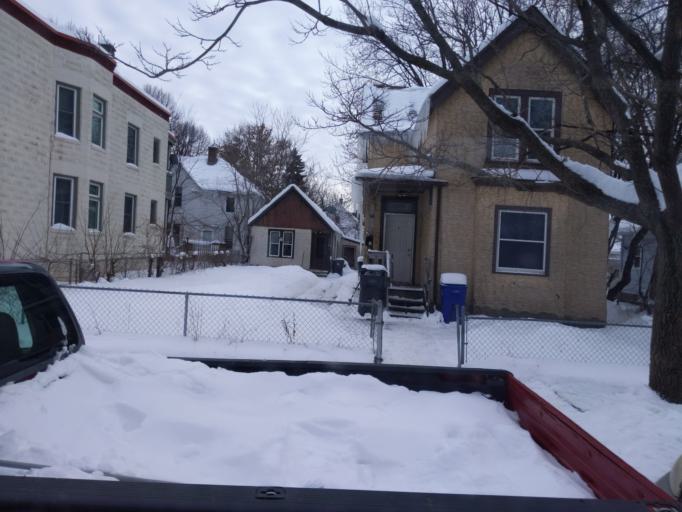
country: US
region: Minnesota
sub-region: Ramsey County
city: Saint Paul
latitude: 44.9594
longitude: -93.1124
